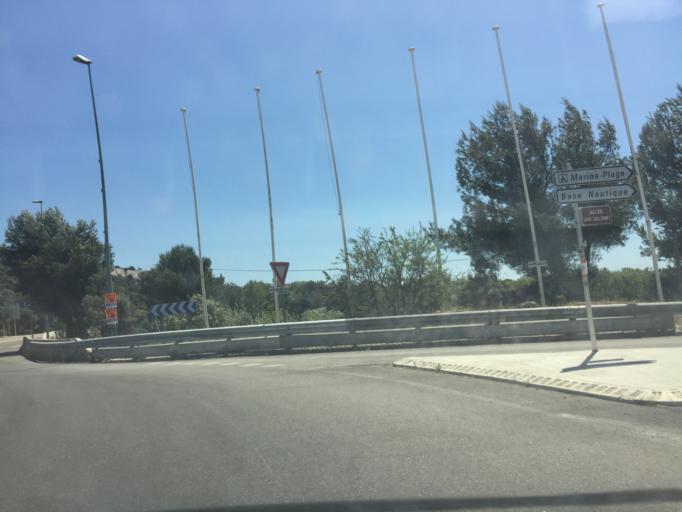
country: FR
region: Provence-Alpes-Cote d'Azur
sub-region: Departement des Bouches-du-Rhone
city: Rognac
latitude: 43.4706
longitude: 5.2311
